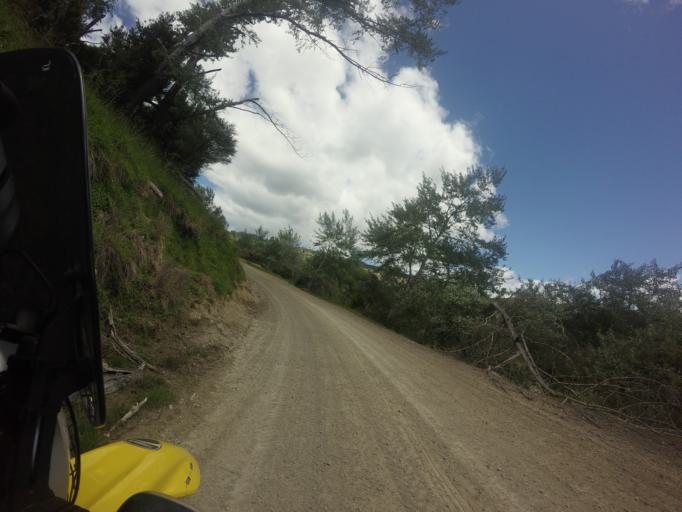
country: NZ
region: Hawke's Bay
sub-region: Wairoa District
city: Wairoa
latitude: -38.9860
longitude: 177.7529
